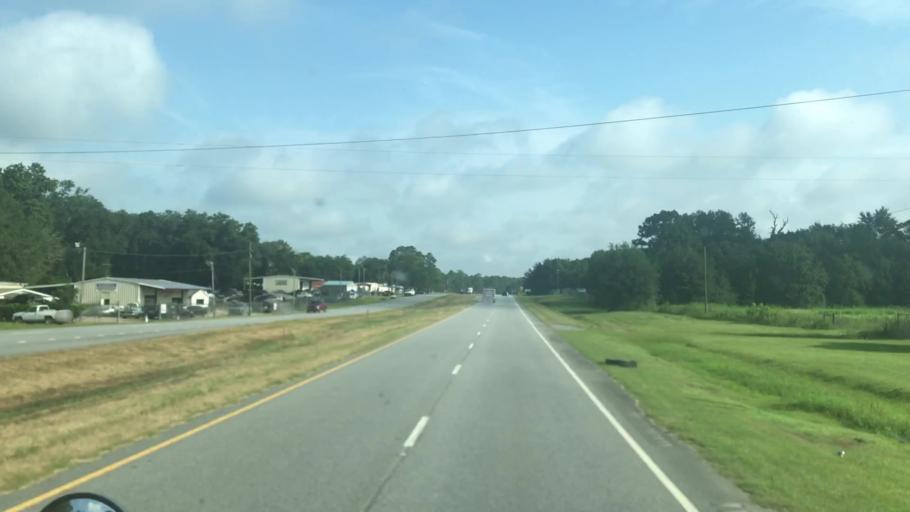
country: US
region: Georgia
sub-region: Decatur County
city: Bainbridge
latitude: 30.9418
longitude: -84.6095
